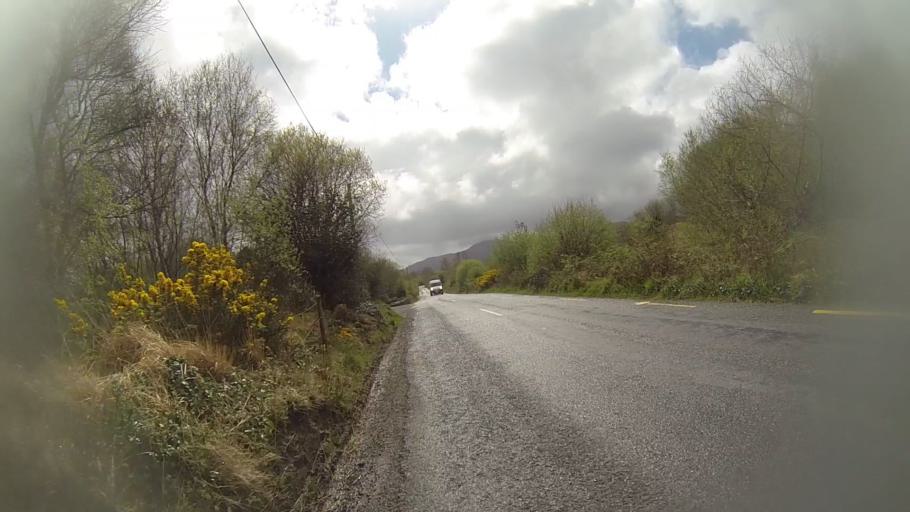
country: IE
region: Munster
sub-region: Ciarrai
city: Killorglin
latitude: 51.8430
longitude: -9.8915
